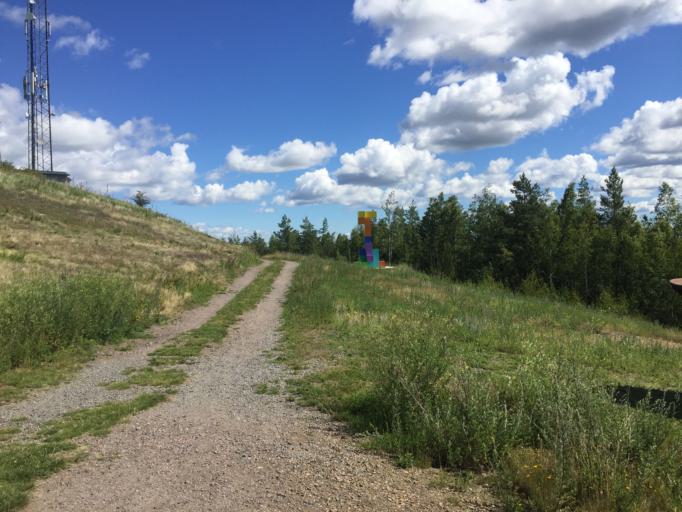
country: SE
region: OErebro
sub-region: Kumla Kommun
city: Hallabrottet
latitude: 59.1255
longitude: 15.2534
